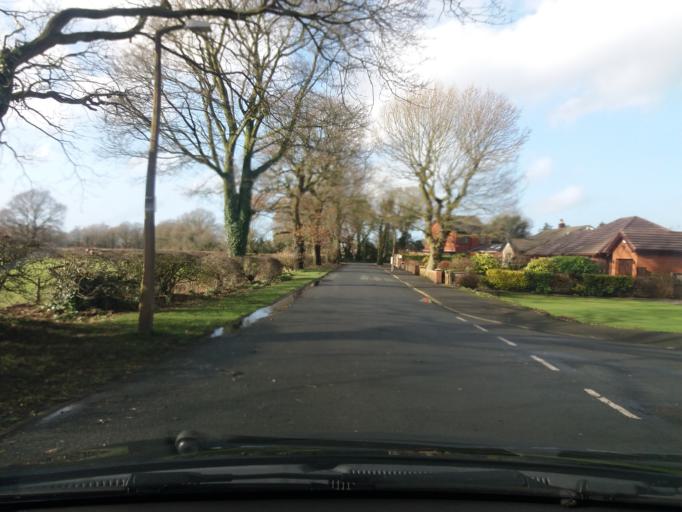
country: GB
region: England
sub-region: Lancashire
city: Adlington
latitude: 53.6063
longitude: -2.6145
